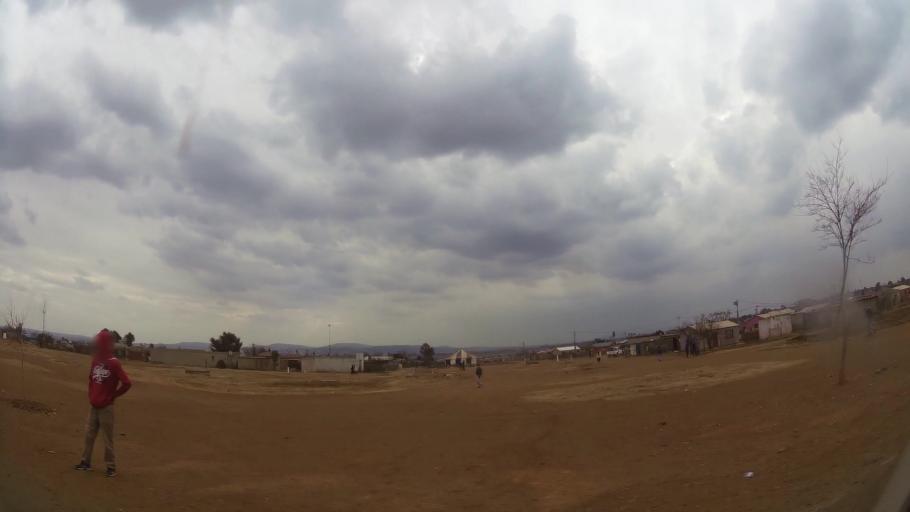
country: ZA
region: Gauteng
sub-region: Ekurhuleni Metropolitan Municipality
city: Germiston
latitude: -26.3898
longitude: 28.1347
